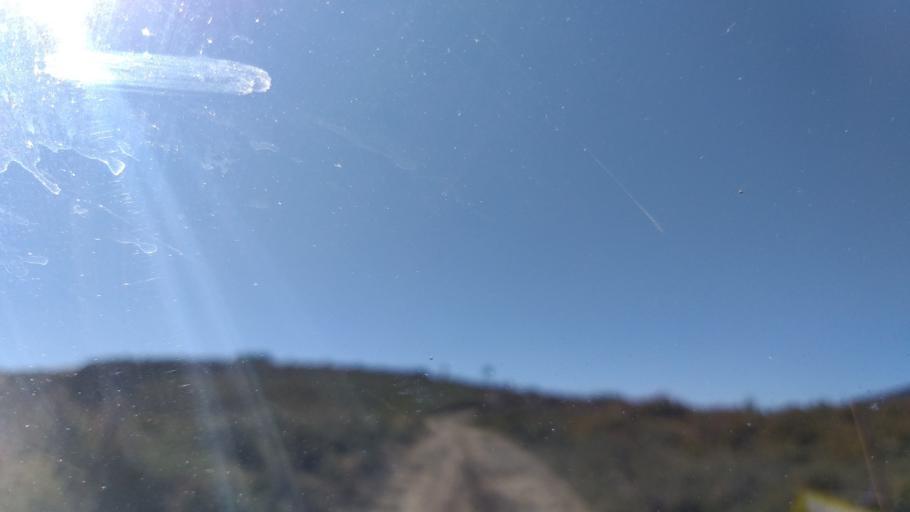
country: PT
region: Guarda
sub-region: Manteigas
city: Manteigas
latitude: 40.4496
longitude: -7.5002
